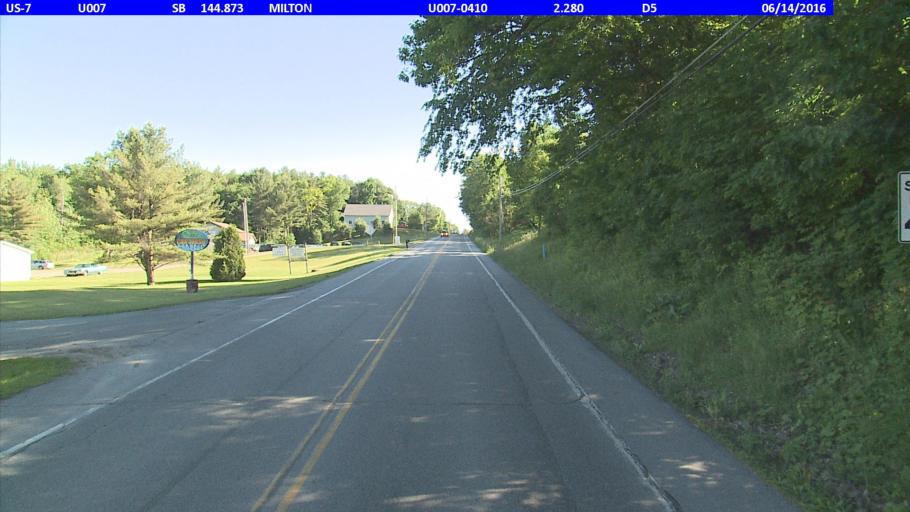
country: US
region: Vermont
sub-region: Chittenden County
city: Milton
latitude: 44.6256
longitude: -73.1465
